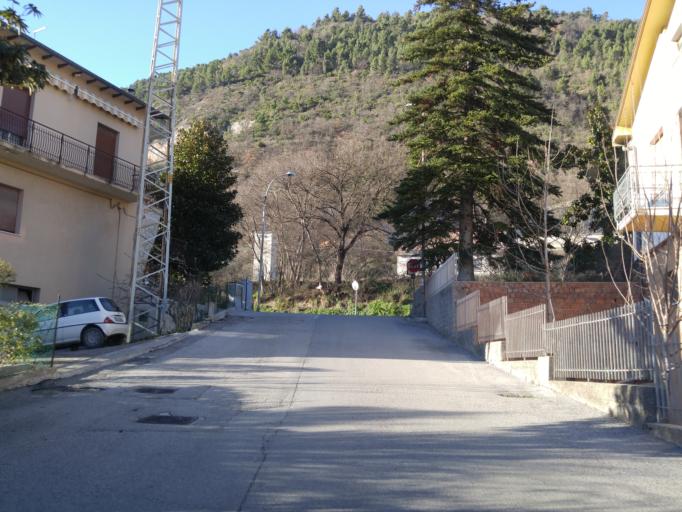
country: IT
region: The Marches
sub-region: Provincia di Pesaro e Urbino
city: Fossombrone
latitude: 43.6860
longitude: 12.7953
